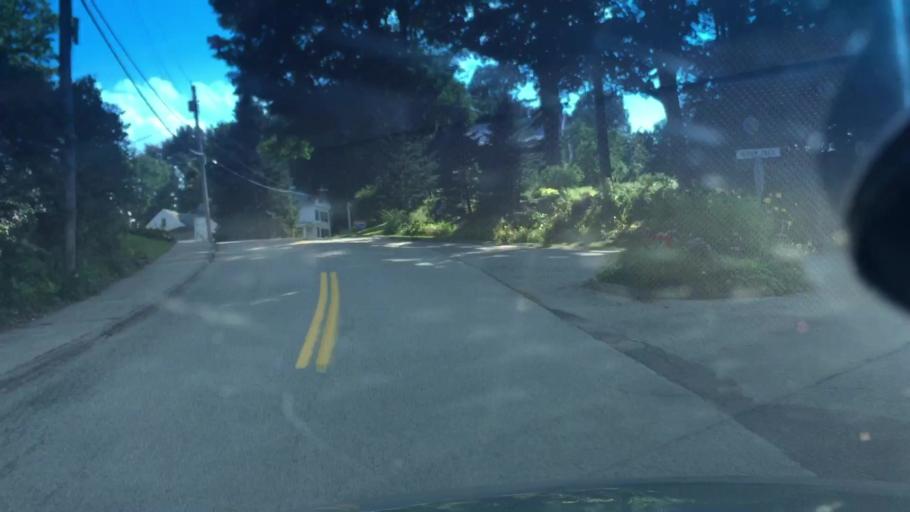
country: US
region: Maine
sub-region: York County
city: York Harbor
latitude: 43.1411
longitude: -70.6551
